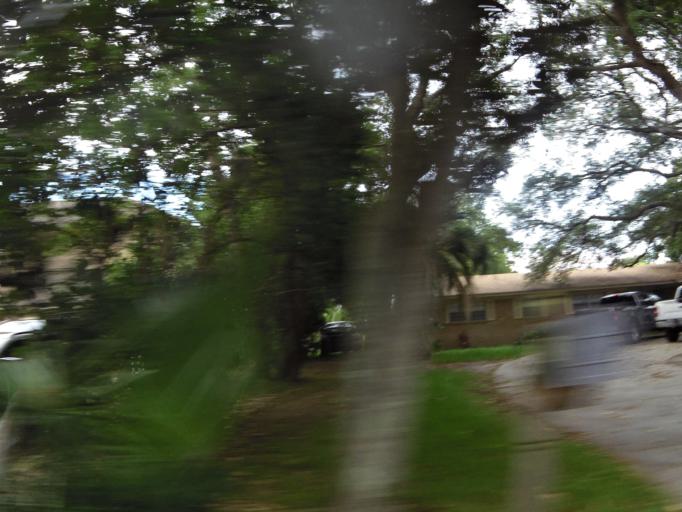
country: US
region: Florida
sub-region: Duval County
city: Jacksonville Beach
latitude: 30.2776
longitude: -81.4034
